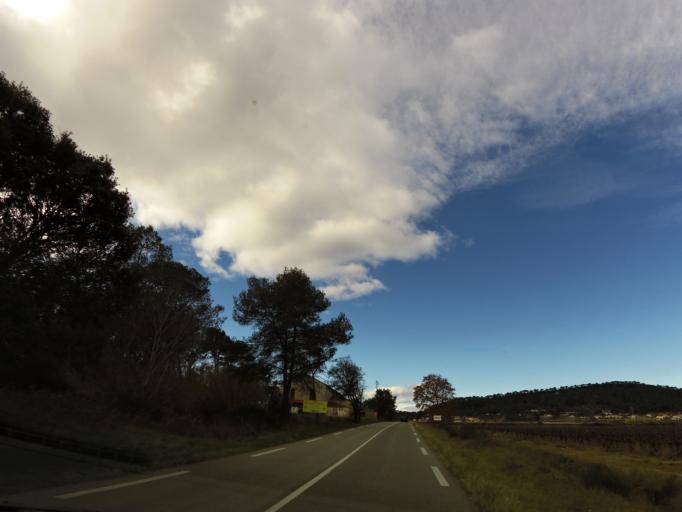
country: FR
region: Languedoc-Roussillon
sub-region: Departement du Gard
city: Sommieres
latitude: 43.8349
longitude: 4.0356
